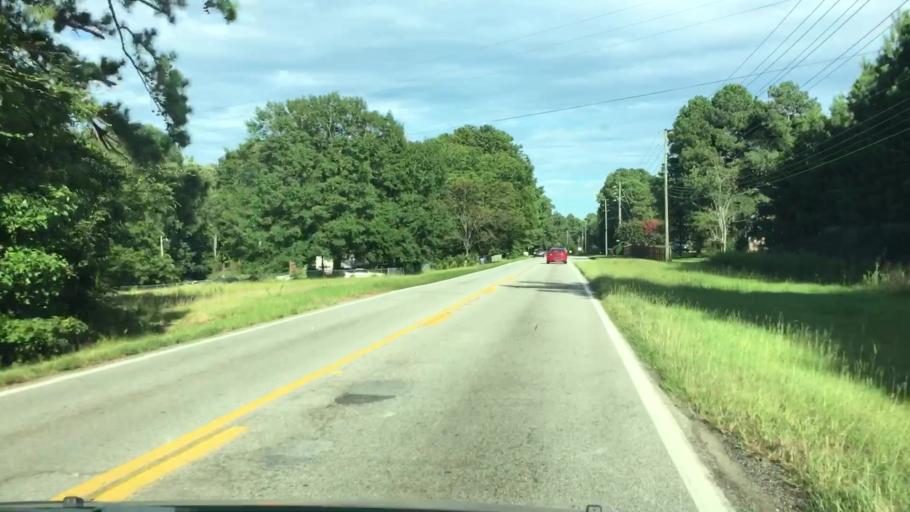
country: US
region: Georgia
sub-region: Henry County
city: Stockbridge
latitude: 33.6063
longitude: -84.2184
